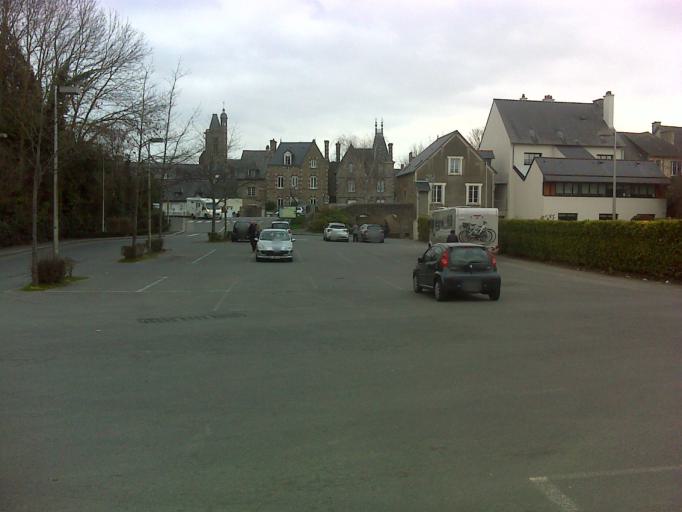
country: FR
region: Brittany
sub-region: Departement d'Ille-et-Vilaine
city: Dol-de-Bretagne
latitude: 48.5477
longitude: -1.7548
